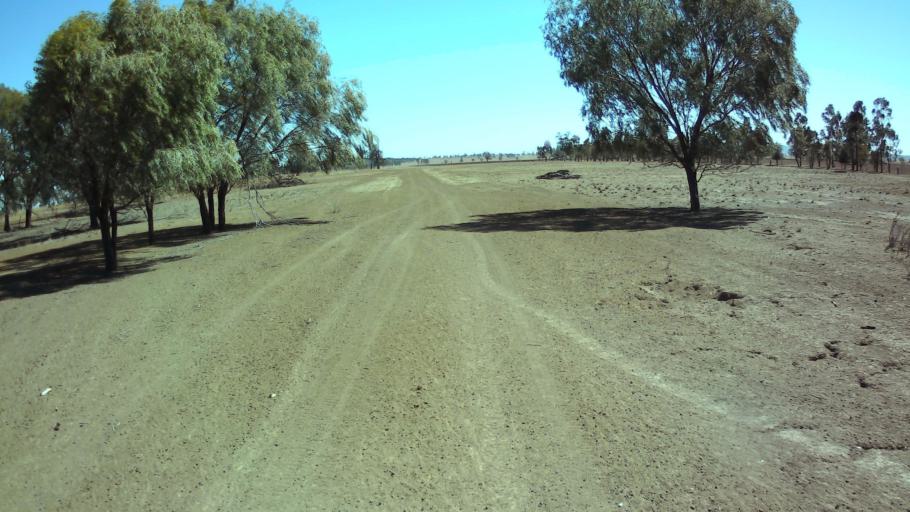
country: AU
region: New South Wales
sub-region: Forbes
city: Forbes
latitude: -33.7153
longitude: 147.6670
